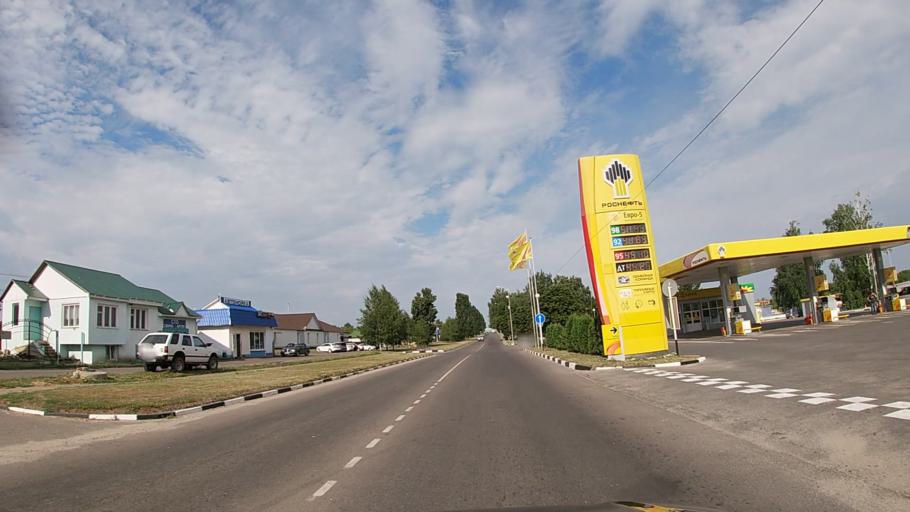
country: RU
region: Belgorod
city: Krasnaya Yaruga
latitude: 50.7981
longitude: 35.6421
